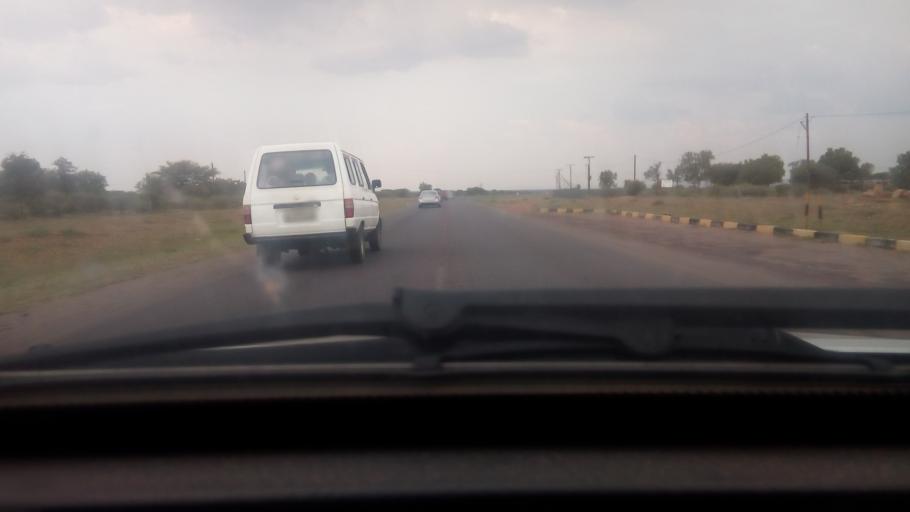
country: BW
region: Kweneng
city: Molepolole
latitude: -24.4542
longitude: 25.6496
